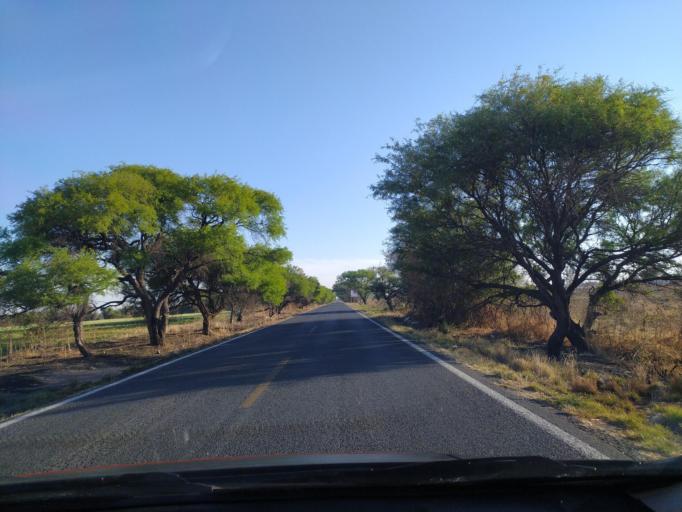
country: MX
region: Guanajuato
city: San Roque
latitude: 20.9575
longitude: -101.8494
